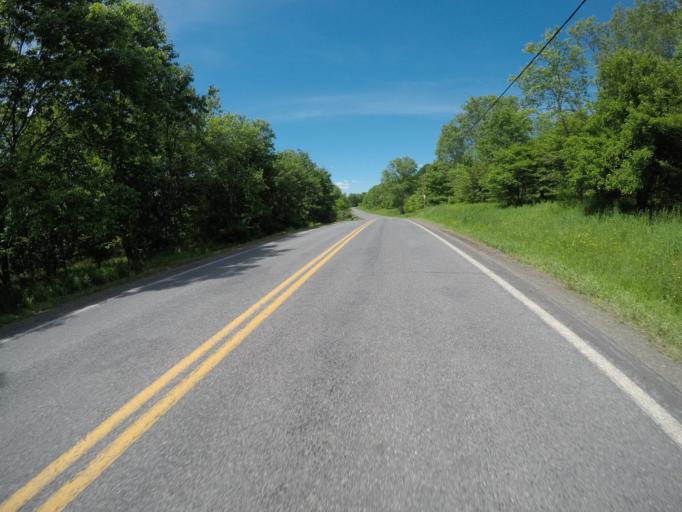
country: US
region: New York
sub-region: Delaware County
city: Delhi
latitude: 42.1531
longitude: -74.7977
